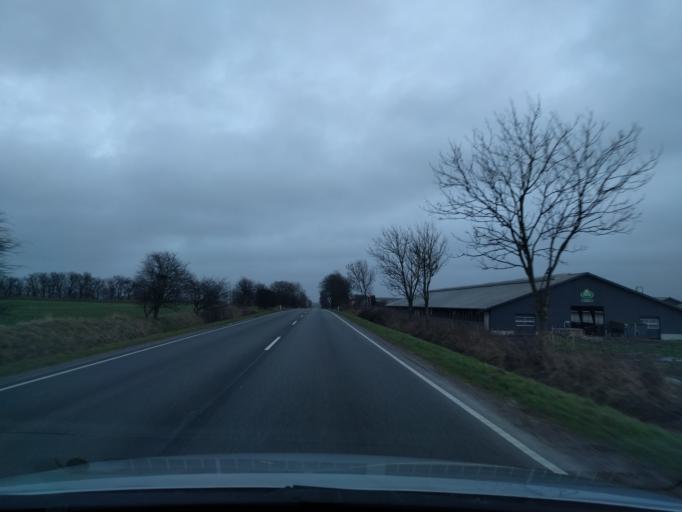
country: DK
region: South Denmark
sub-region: Tonder Kommune
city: Toftlund
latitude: 55.2510
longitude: 9.1644
